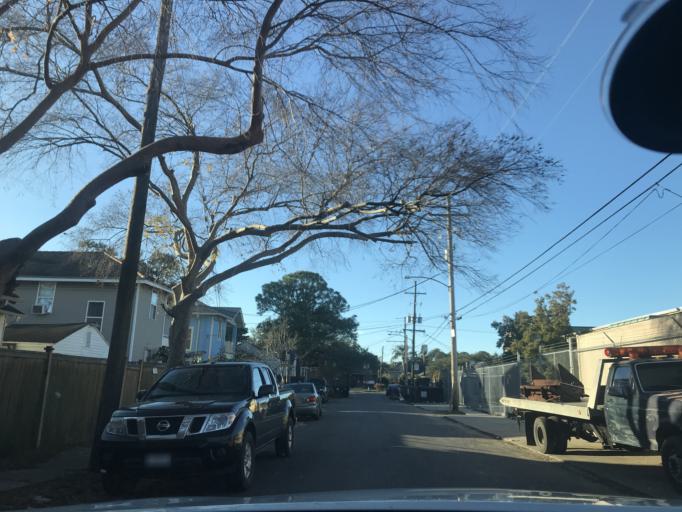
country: US
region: Louisiana
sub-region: Orleans Parish
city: New Orleans
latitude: 29.9546
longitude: -90.1050
